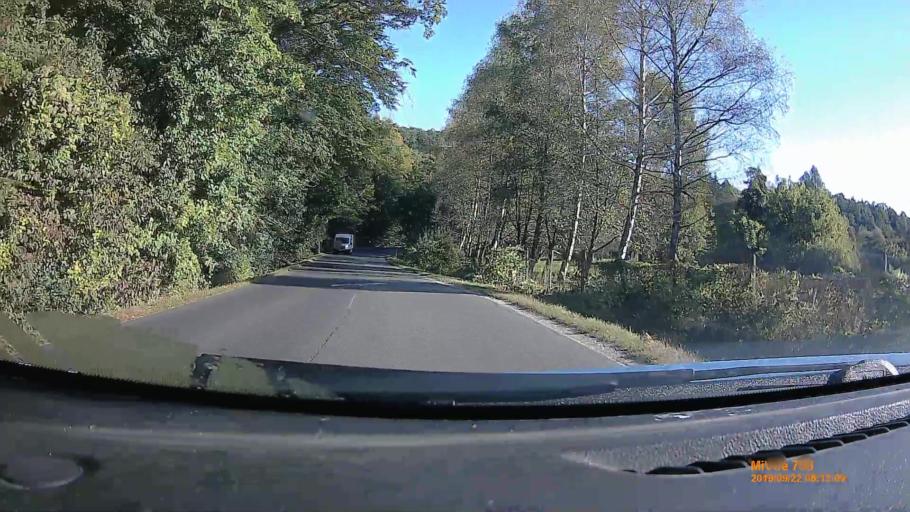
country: HU
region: Borsod-Abauj-Zemplen
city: Sajobabony
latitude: 48.1151
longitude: 20.6541
